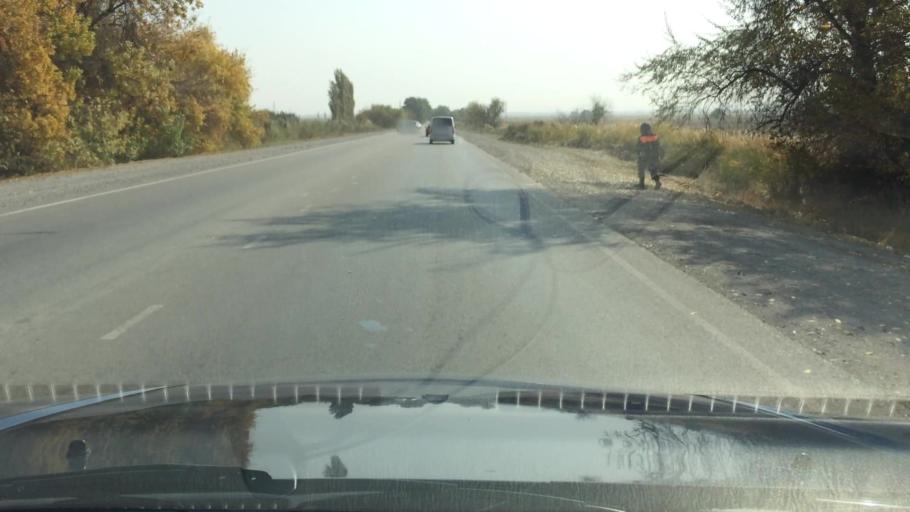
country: KG
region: Chuy
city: Lebedinovka
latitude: 42.9261
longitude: 74.6992
